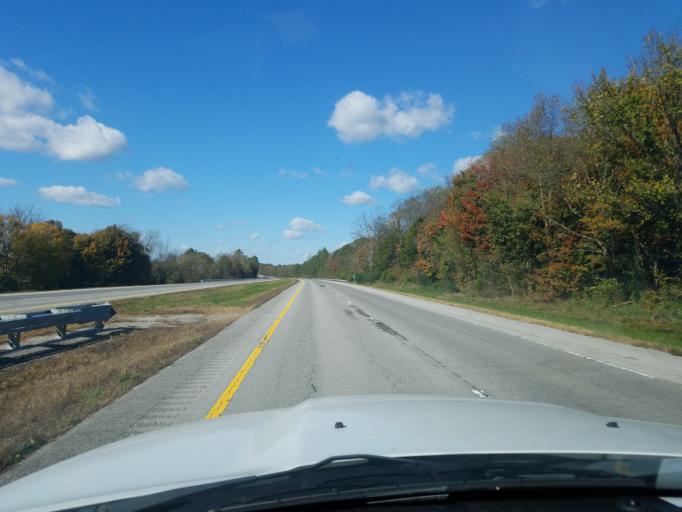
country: US
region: Kentucky
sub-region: Metcalfe County
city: Edmonton
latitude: 36.9982
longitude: -85.7188
